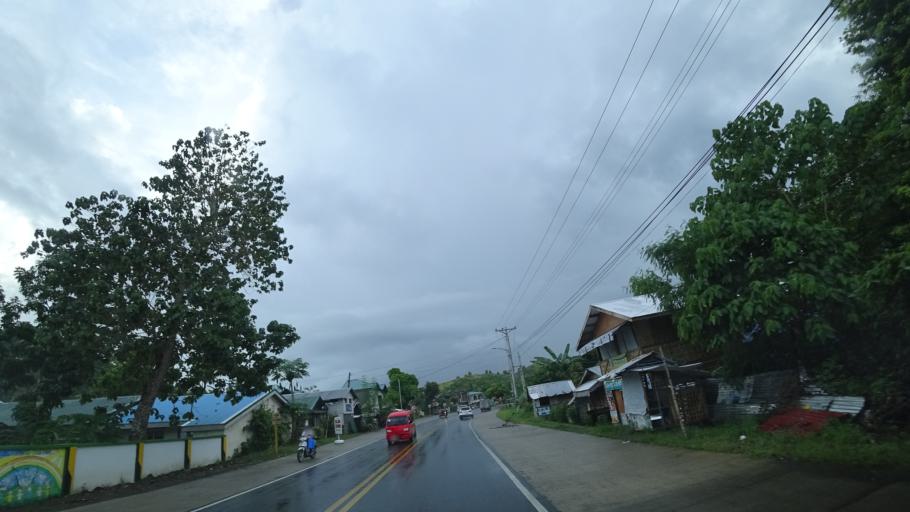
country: PH
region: Eastern Visayas
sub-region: Province of Leyte
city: Kabuynan
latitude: 11.0818
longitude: 125.0252
